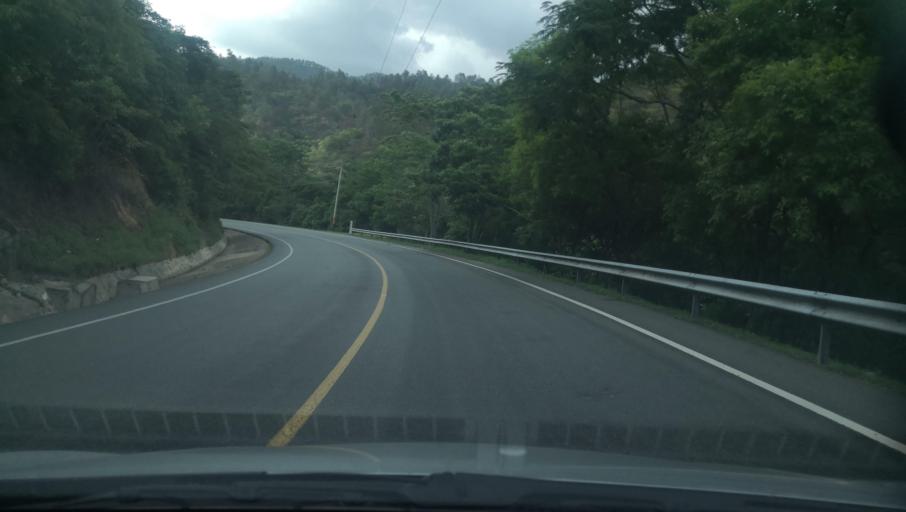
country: NI
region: Nueva Segovia
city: Mozonte
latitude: 13.6951
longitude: -86.4870
